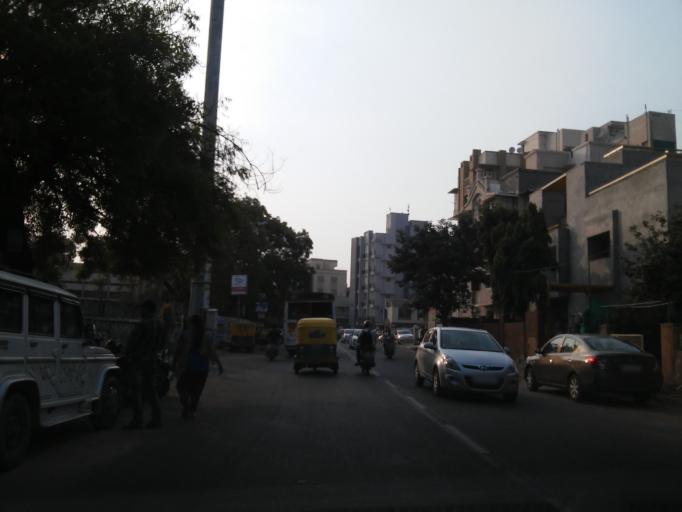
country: IN
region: Gujarat
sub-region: Ahmadabad
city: Ahmedabad
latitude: 23.0099
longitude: 72.5534
